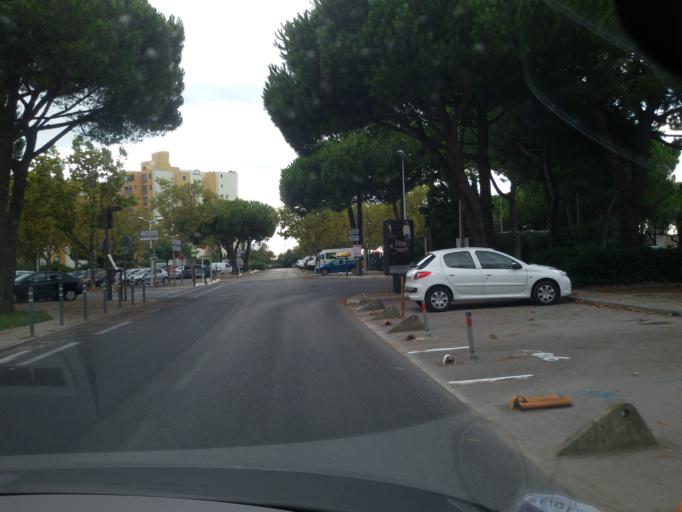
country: FR
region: Languedoc-Roussillon
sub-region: Departement de l'Herault
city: Perols
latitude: 43.5480
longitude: 3.9750
